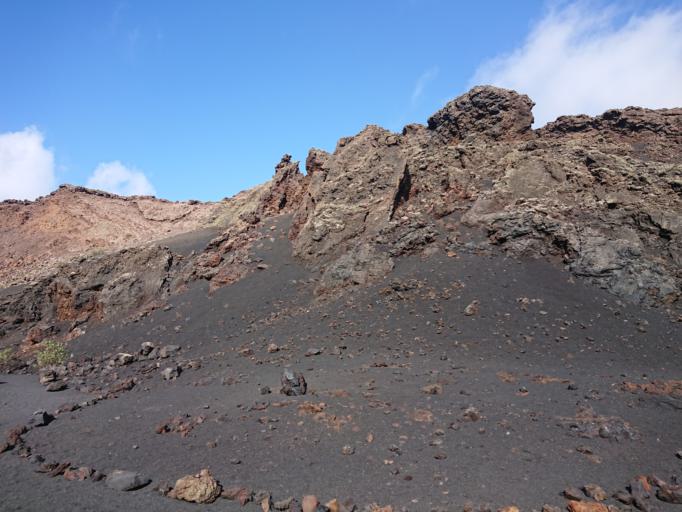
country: ES
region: Canary Islands
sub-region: Provincia de Las Palmas
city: Tias
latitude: 28.9920
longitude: -13.6920
